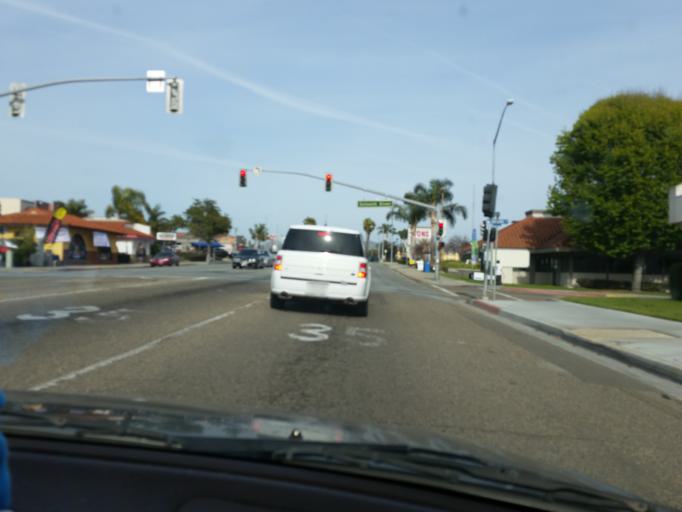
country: US
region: California
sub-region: San Luis Obispo County
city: Grover Beach
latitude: 35.1211
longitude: -120.6121
